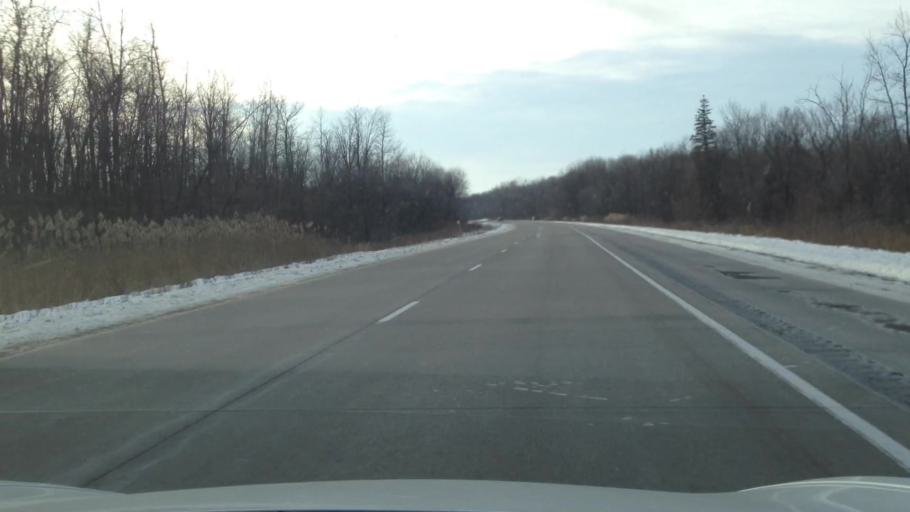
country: CA
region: Ontario
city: Hawkesbury
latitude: 45.4490
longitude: -74.7140
